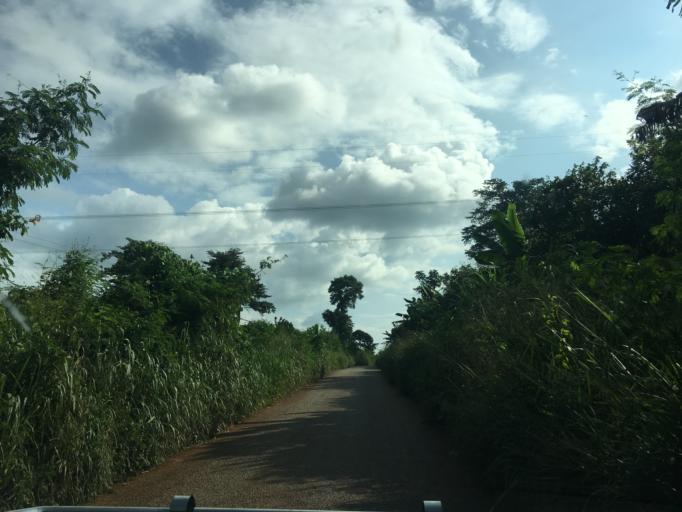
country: GH
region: Western
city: Bibiani
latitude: 6.7937
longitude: -2.5321
